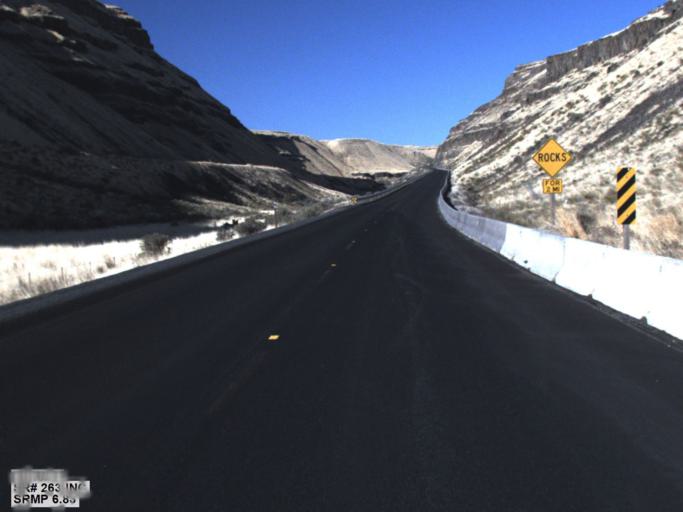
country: US
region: Washington
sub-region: Franklin County
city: Connell
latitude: 46.6124
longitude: -118.5549
